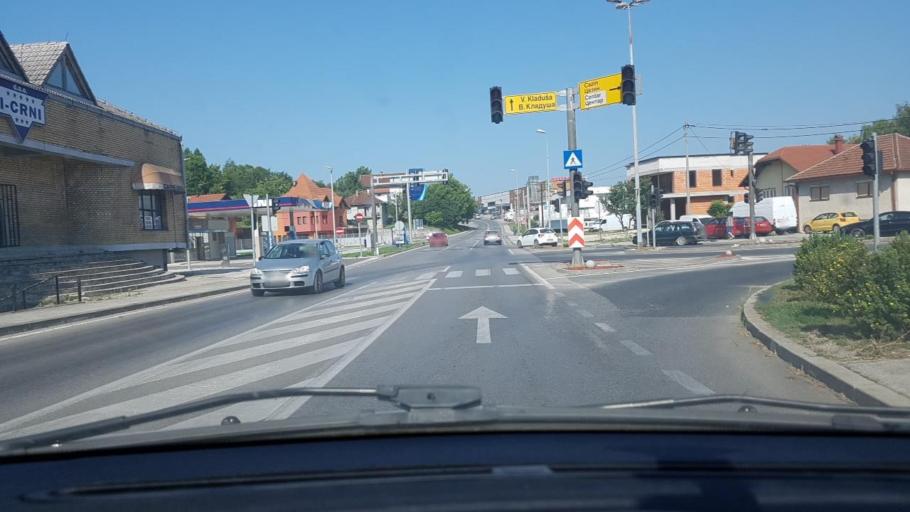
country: BA
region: Federation of Bosnia and Herzegovina
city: Cazin
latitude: 44.9652
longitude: 15.9235
